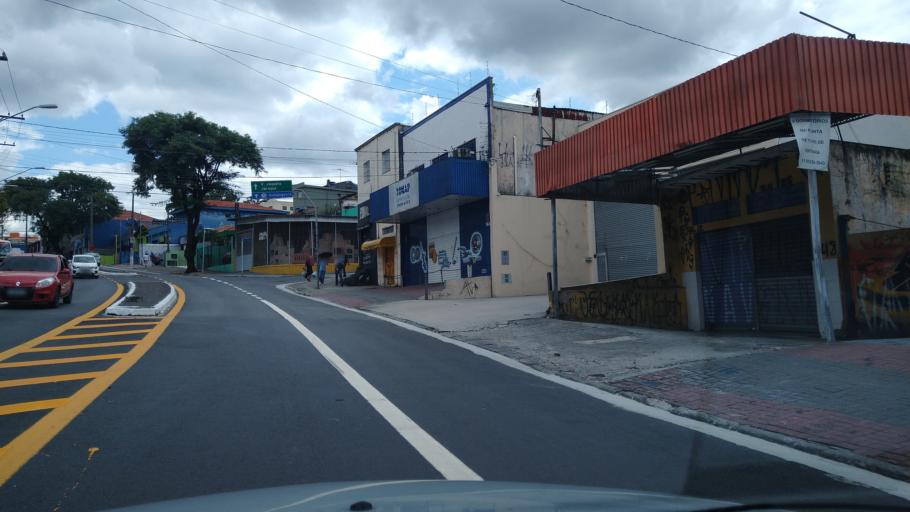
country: BR
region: Sao Paulo
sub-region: Osasco
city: Osasco
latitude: -23.4884
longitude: -46.7303
